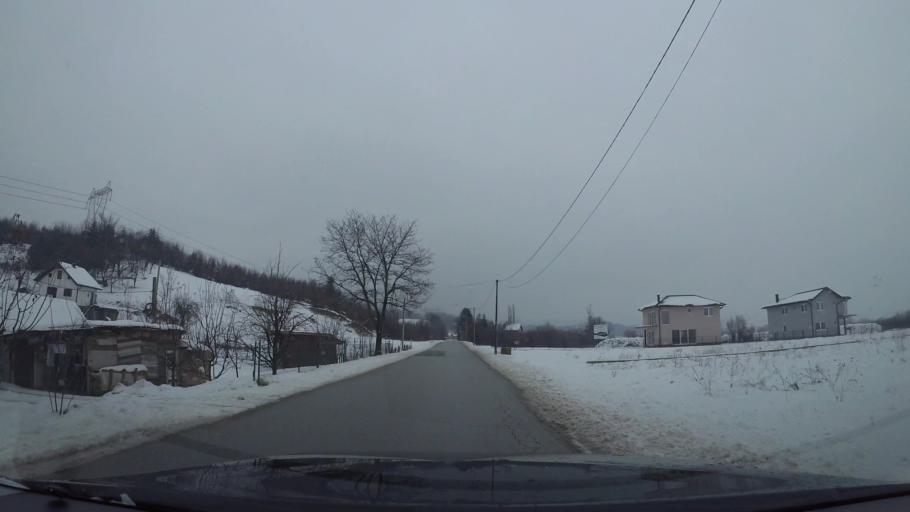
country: BA
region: Federation of Bosnia and Herzegovina
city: Hadzici
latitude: 43.8573
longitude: 18.2726
